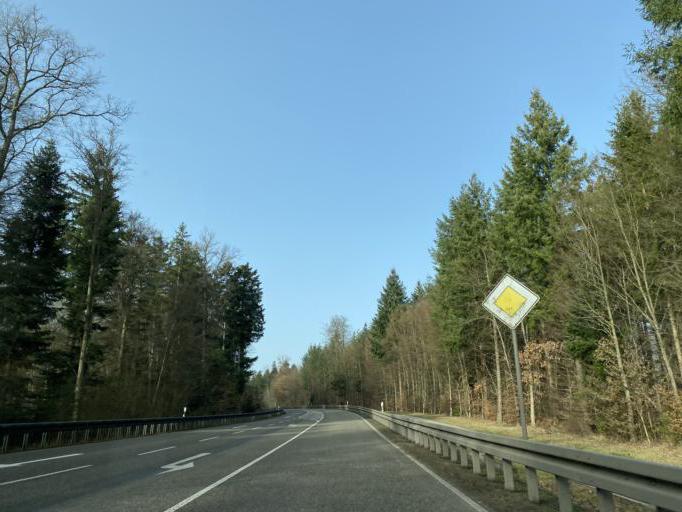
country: DE
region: Baden-Wuerttemberg
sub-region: Karlsruhe Region
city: Wurmberg
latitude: 48.8796
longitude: 8.7819
